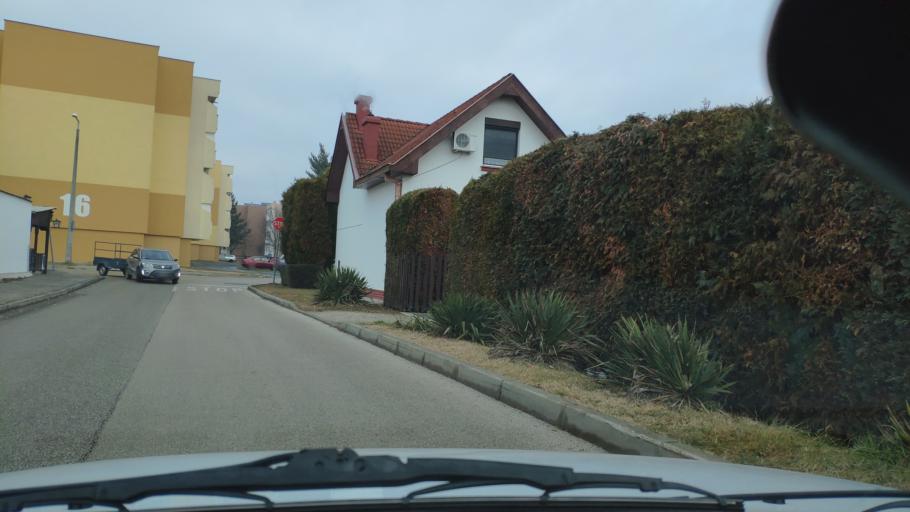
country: HU
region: Zala
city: Nagykanizsa
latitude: 46.4570
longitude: 17.0156
